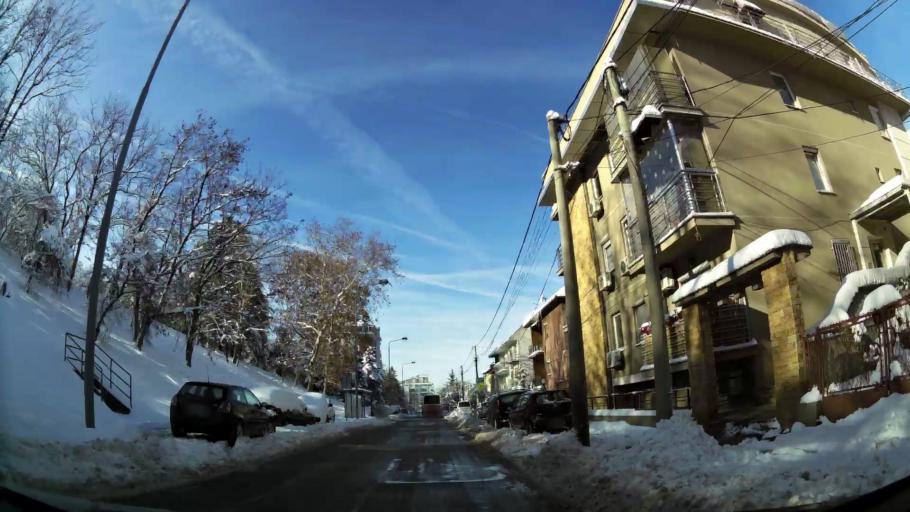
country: RS
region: Central Serbia
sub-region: Belgrade
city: Zvezdara
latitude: 44.7852
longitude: 20.5081
